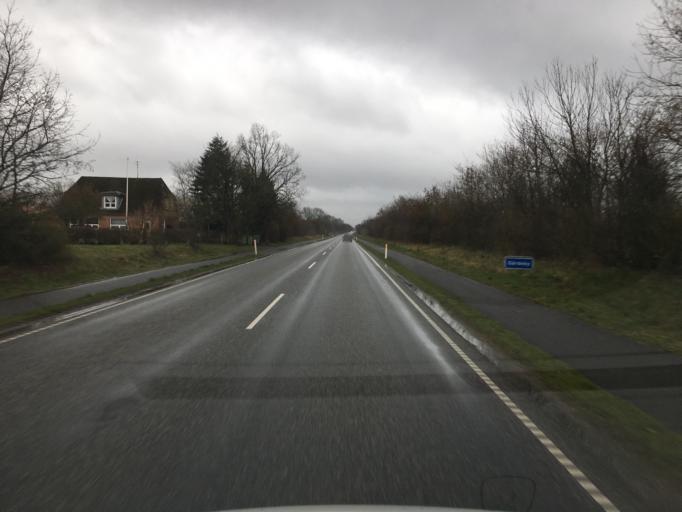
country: DK
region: South Denmark
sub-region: Aabenraa Kommune
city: Tinglev
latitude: 54.9088
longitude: 9.2539
